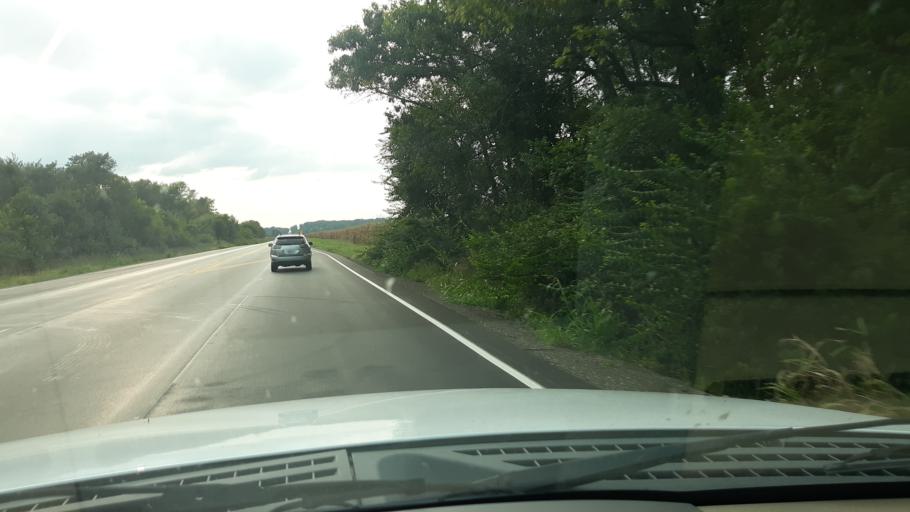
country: US
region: Indiana
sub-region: Gibson County
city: Princeton
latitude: 38.3557
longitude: -87.6263
